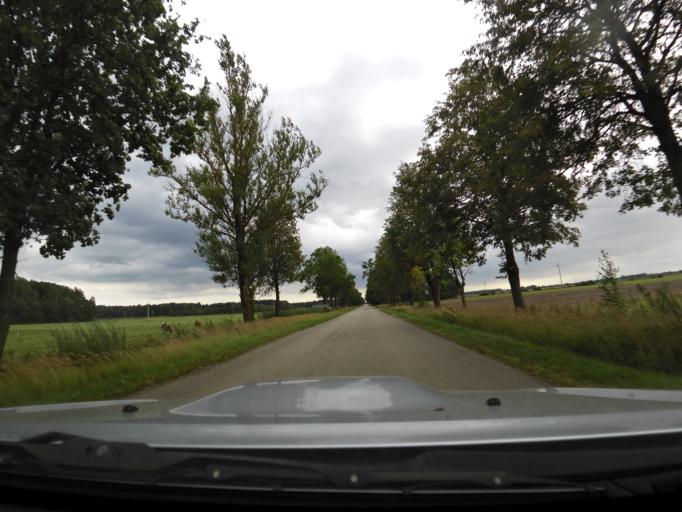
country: LT
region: Panevezys
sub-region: Birzai
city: Birzai
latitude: 56.3695
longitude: 24.7816
